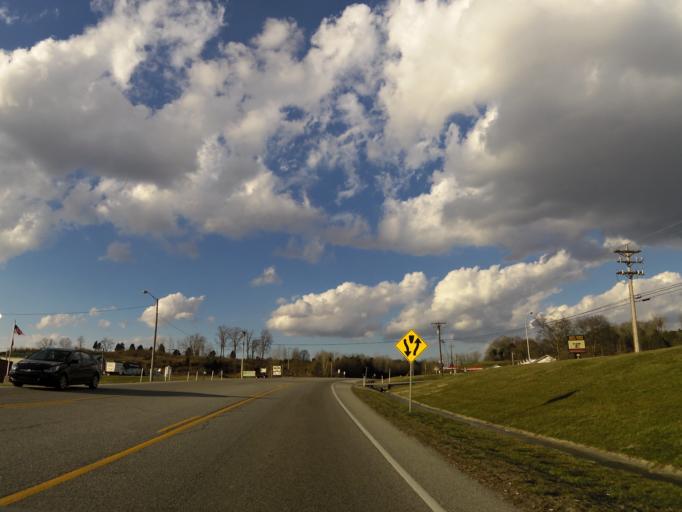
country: US
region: Tennessee
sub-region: Smith County
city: South Carthage
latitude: 36.2252
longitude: -85.9491
